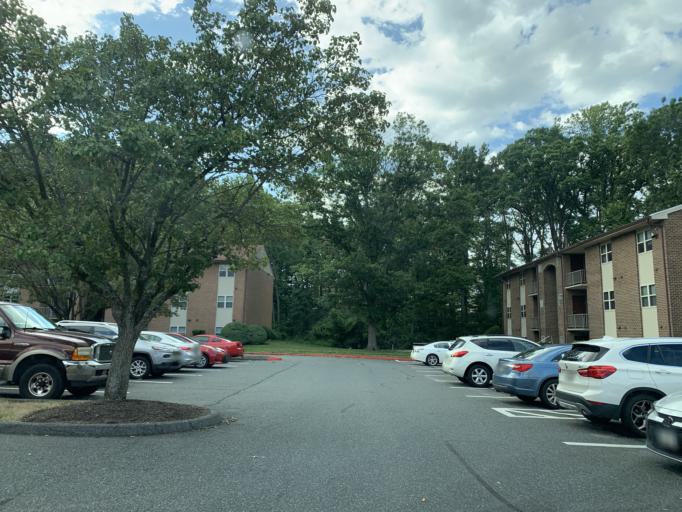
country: US
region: Maryland
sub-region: Harford County
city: Edgewood
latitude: 39.4625
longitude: -76.3035
